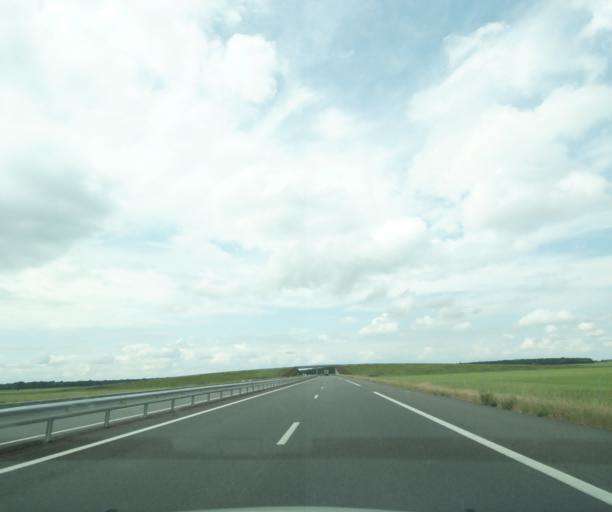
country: FR
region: Centre
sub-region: Departement du Cher
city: Levet
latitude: 46.8609
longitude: 2.4282
